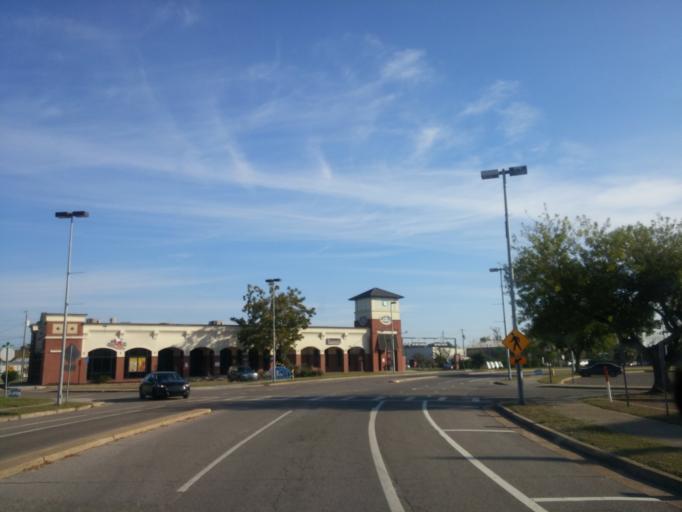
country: US
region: Mississippi
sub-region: Harrison County
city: Biloxi
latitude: 30.3975
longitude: -88.8903
